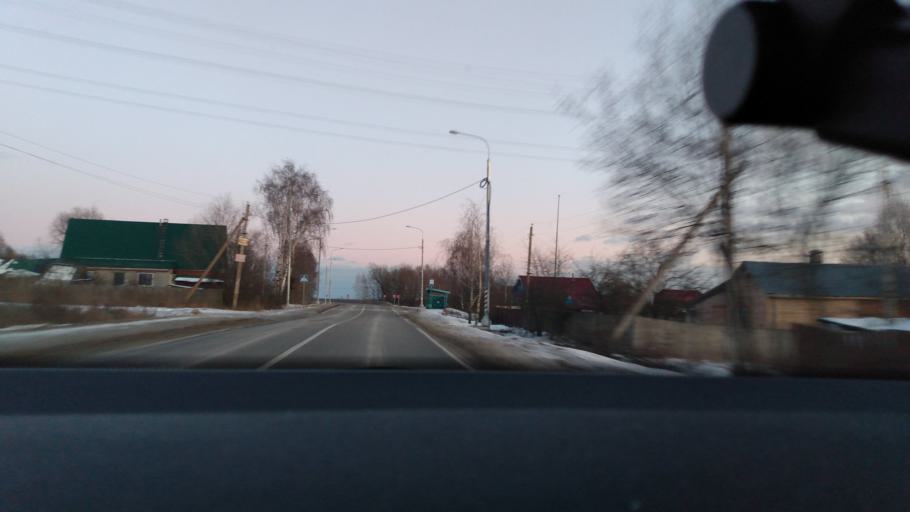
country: RU
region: Moskovskaya
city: Krasnaya Poyma
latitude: 55.1375
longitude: 39.1292
